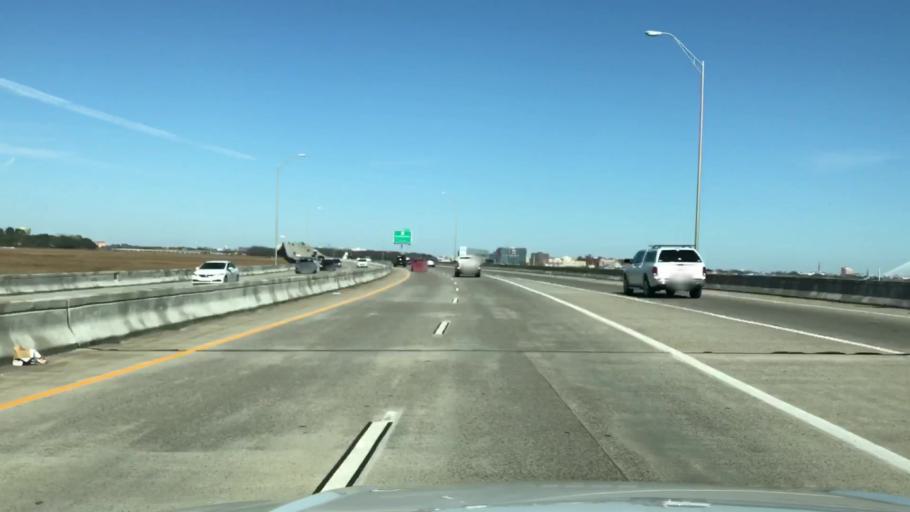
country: US
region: South Carolina
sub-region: Charleston County
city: Charleston
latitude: 32.7597
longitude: -79.9582
